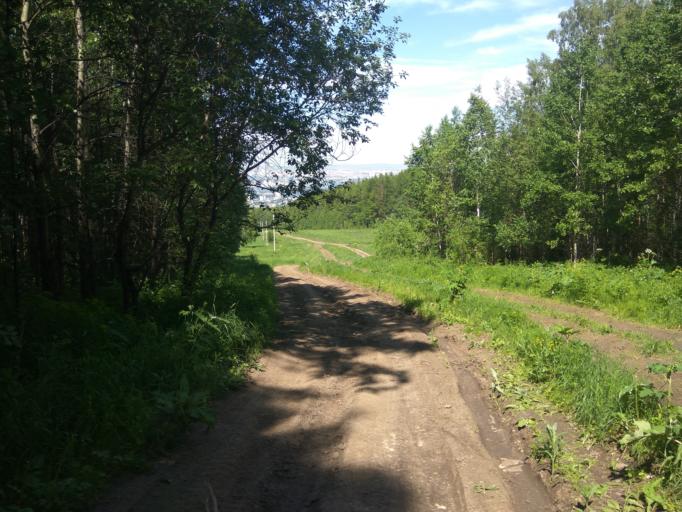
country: RU
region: Krasnoyarskiy
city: Krasnoyarsk
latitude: 55.9542
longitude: 92.8751
